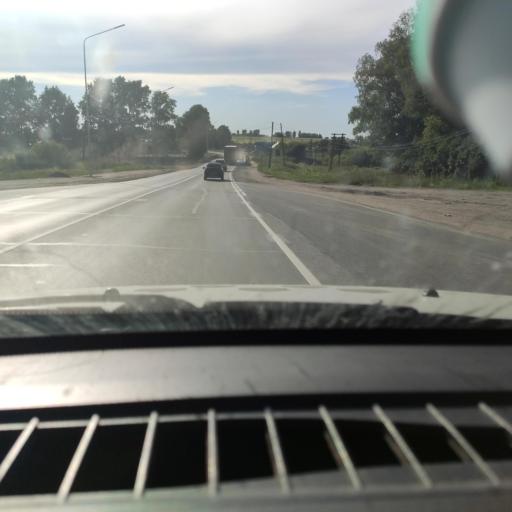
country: RU
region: Kirov
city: Vakhrushi
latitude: 58.6766
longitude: 50.0060
